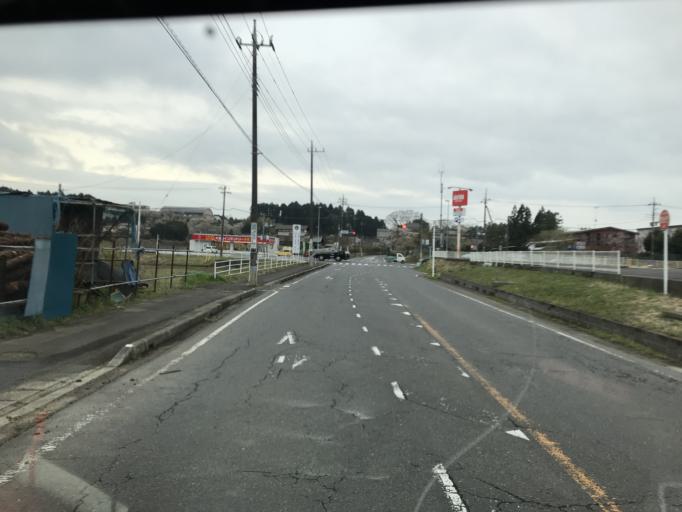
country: JP
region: Chiba
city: Sawara
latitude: 35.8185
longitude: 140.5054
